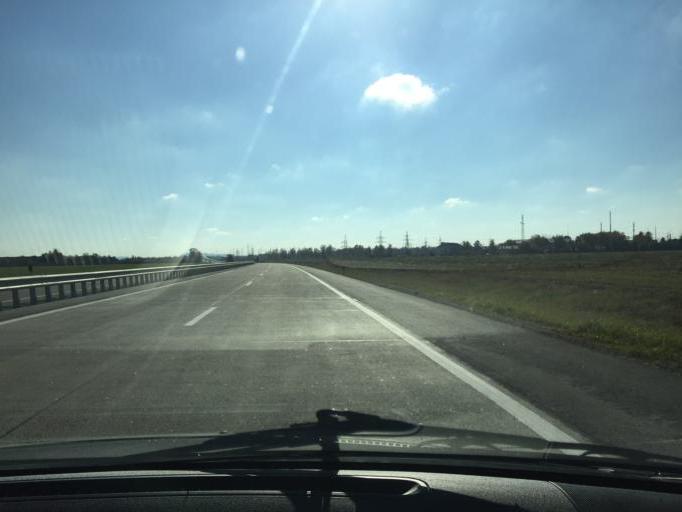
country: BY
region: Minsk
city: Slutsk
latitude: 53.0257
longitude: 27.4843
